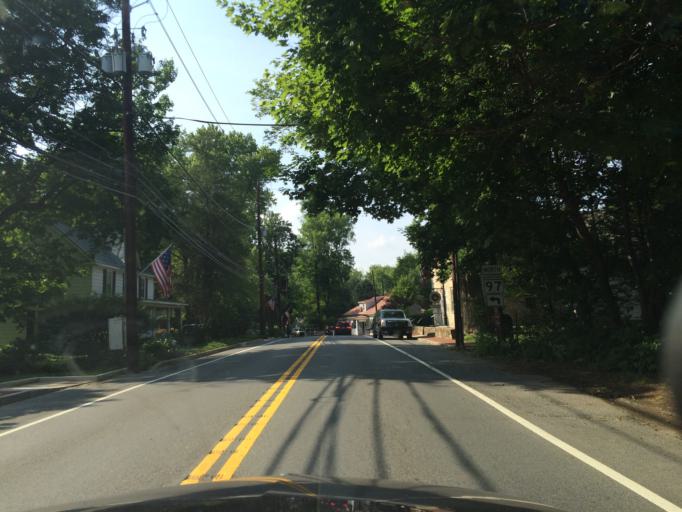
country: US
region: Maryland
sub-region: Montgomery County
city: Olney
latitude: 39.1798
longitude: -77.0584
